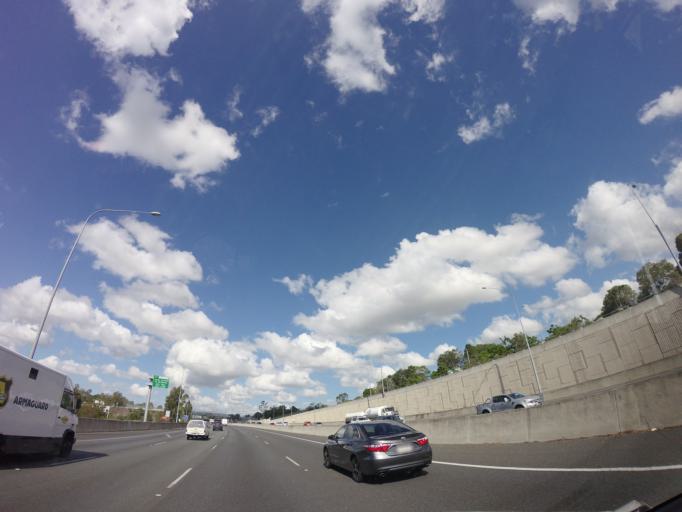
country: AU
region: Queensland
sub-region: Ipswich
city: Goodna
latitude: -27.6085
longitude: 152.9097
